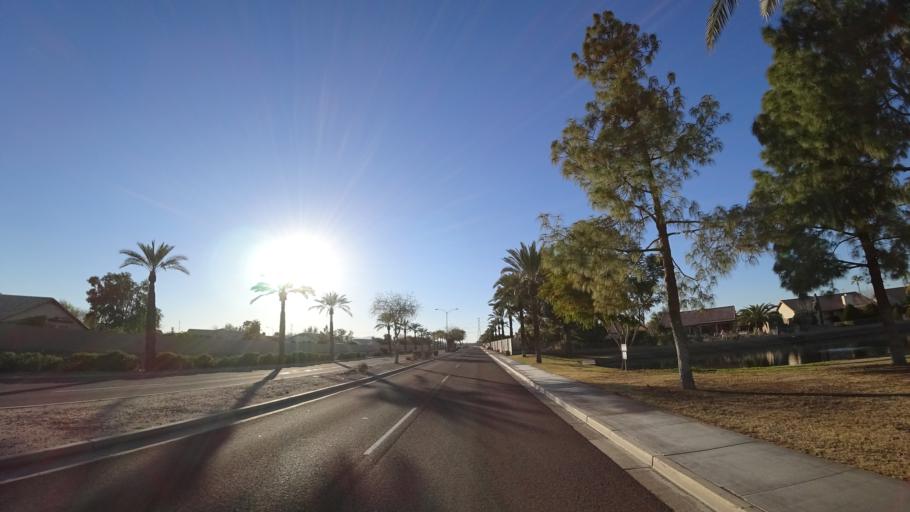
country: US
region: Arizona
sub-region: Maricopa County
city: Sun City West
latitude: 33.6672
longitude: -112.2948
